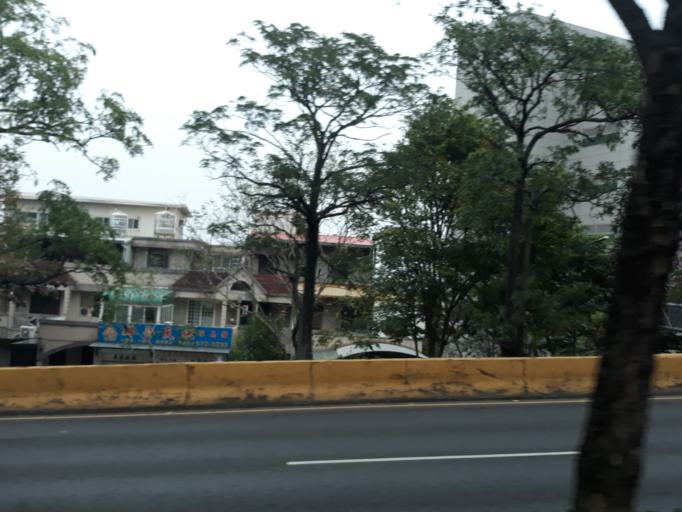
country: TW
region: Taiwan
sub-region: Hsinchu
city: Hsinchu
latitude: 24.8002
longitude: 121.0033
